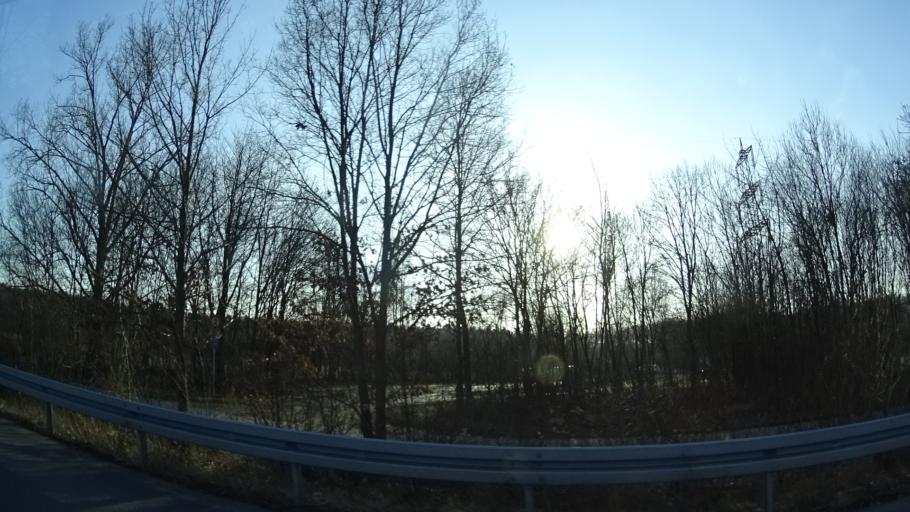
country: DE
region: Hesse
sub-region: Regierungsbezirk Darmstadt
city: Eppertshausen
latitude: 49.9426
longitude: 8.8371
